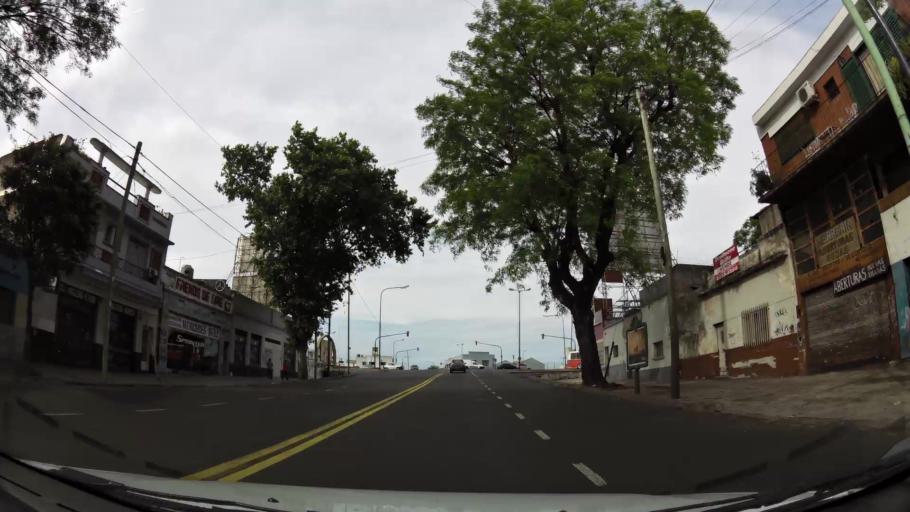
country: AR
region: Buenos Aires F.D.
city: Villa Lugano
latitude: -34.6502
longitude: -58.4702
